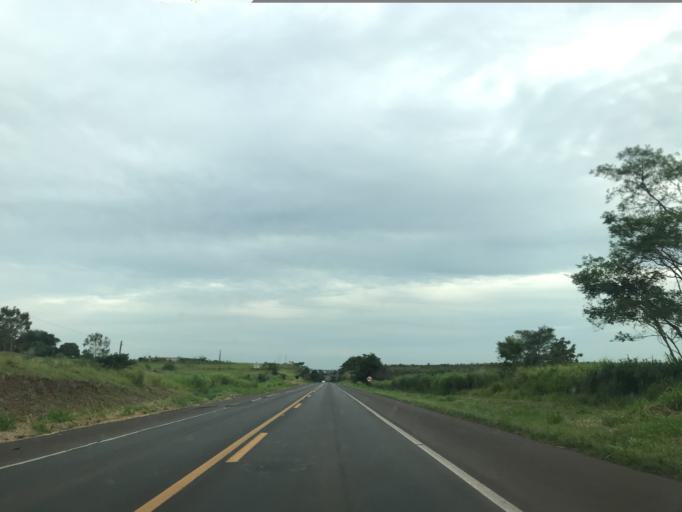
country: BR
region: Sao Paulo
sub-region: Birigui
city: Birigui
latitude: -21.5873
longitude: -50.4575
